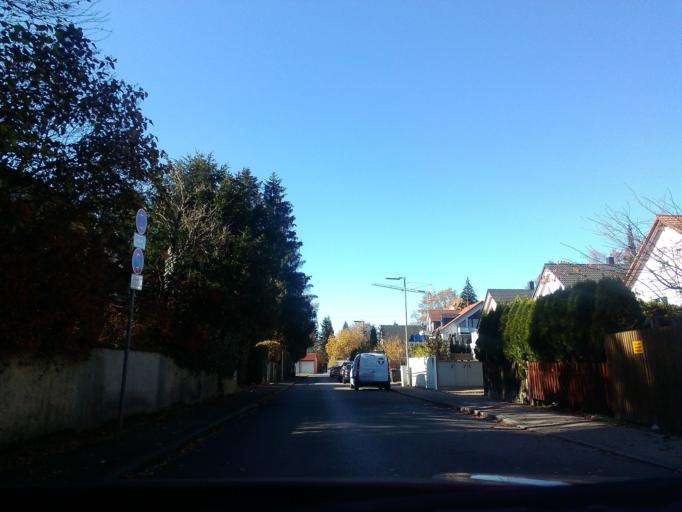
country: DE
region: Bavaria
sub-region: Upper Bavaria
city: Grobenzell
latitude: 48.1793
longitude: 11.4003
